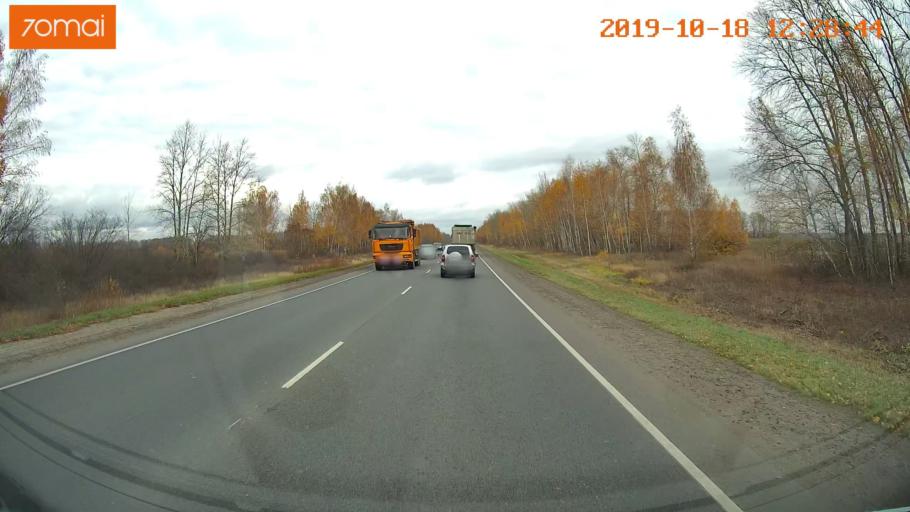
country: RU
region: Rjazan
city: Ryazan'
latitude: 54.5740
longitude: 39.5733
